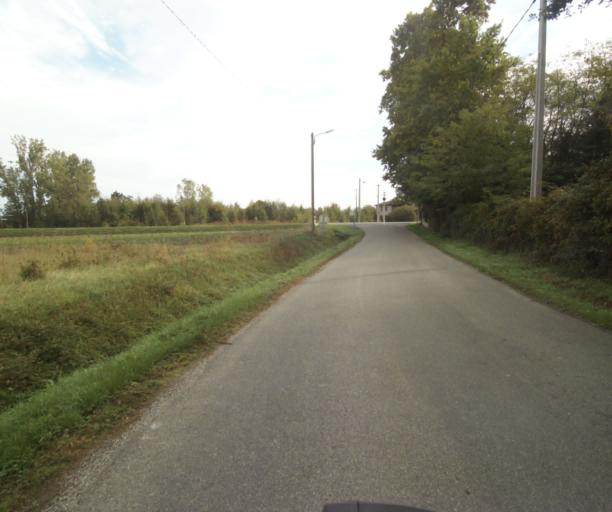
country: FR
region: Midi-Pyrenees
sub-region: Departement du Tarn-et-Garonne
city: Finhan
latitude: 43.9207
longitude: 1.2231
